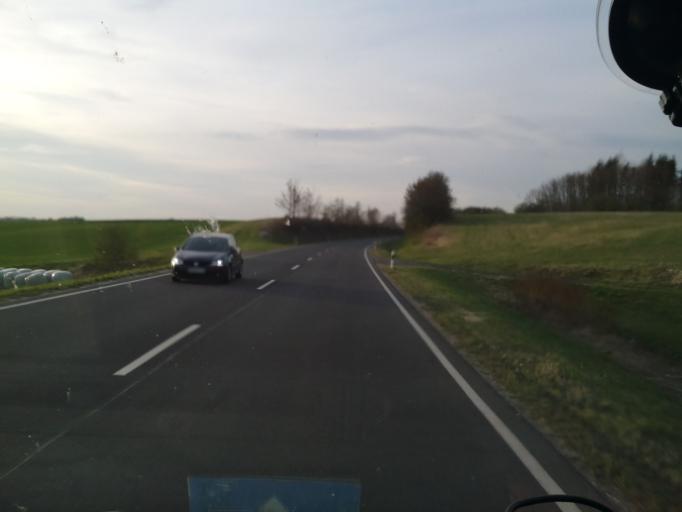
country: DE
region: Bavaria
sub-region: Regierungsbezirk Unterfranken
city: Pfarrweisach
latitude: 50.1191
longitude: 10.7643
